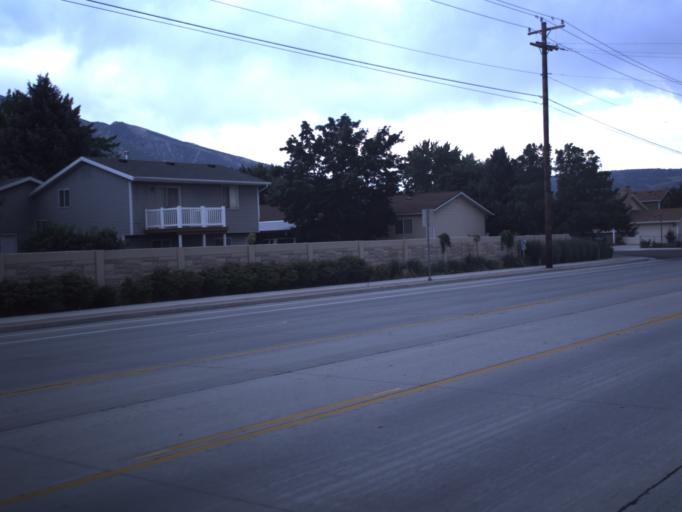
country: US
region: Utah
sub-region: Salt Lake County
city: White City
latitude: 40.5477
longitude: -111.8724
